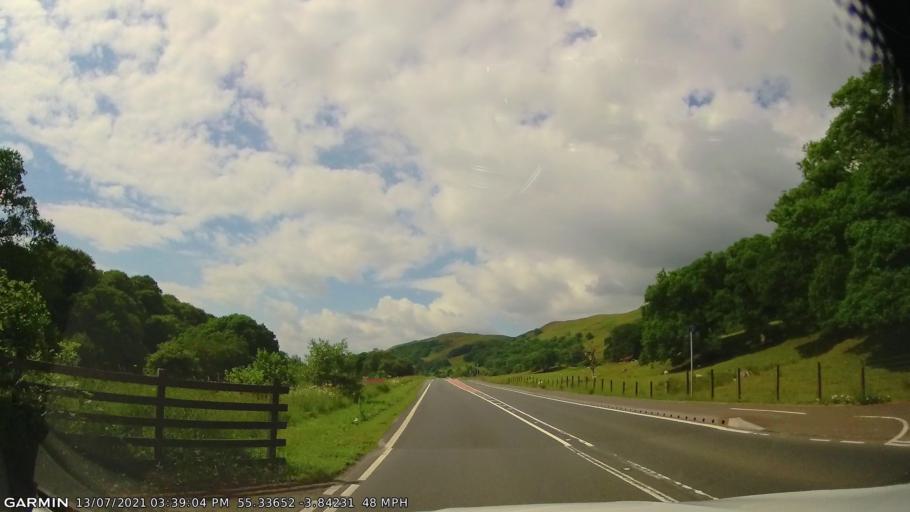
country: GB
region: Scotland
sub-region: Dumfries and Galloway
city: Sanquhar
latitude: 55.3352
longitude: -3.8404
